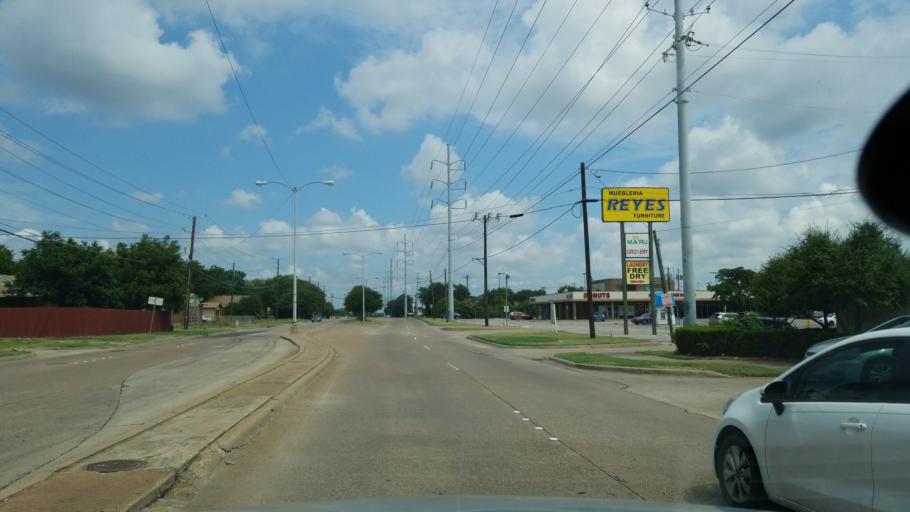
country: US
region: Texas
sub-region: Dallas County
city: Garland
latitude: 32.9168
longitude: -96.6652
